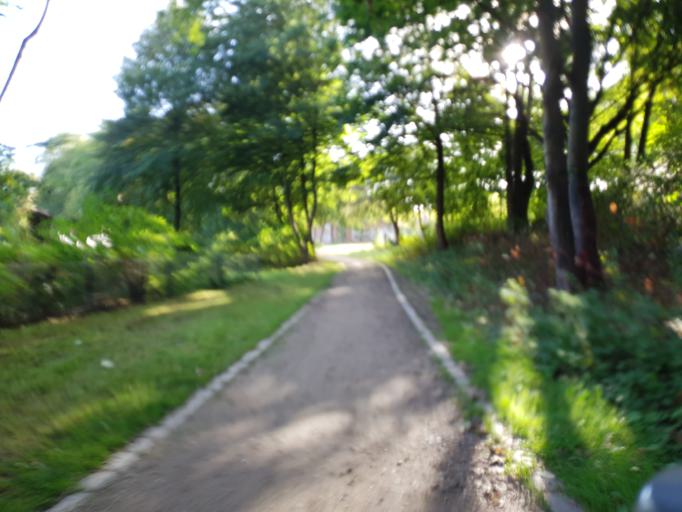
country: DE
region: Schleswig-Holstein
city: Kiel
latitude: 54.3318
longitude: 10.1364
